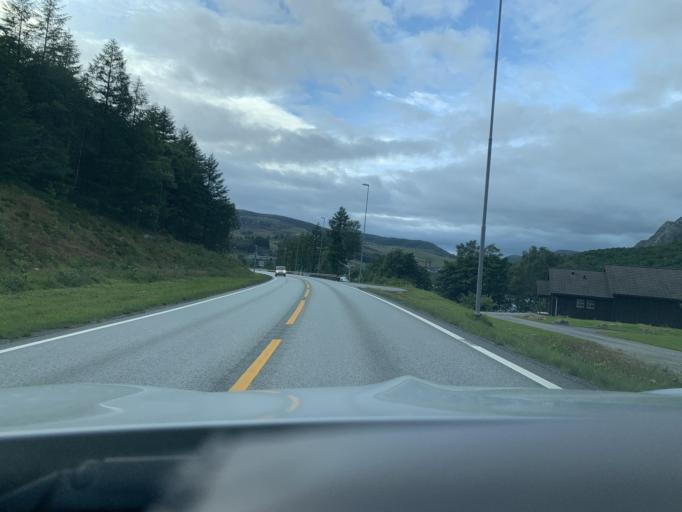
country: NO
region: Rogaland
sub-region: Bjerkreim
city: Vikesa
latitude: 58.6254
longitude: 6.0916
